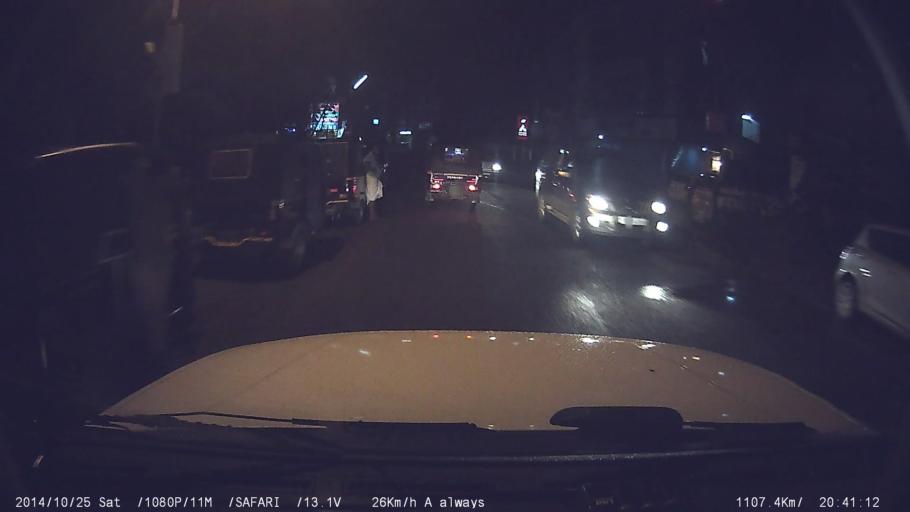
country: IN
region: Kerala
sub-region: Kottayam
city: Kottayam
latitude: 9.6692
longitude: 76.5557
